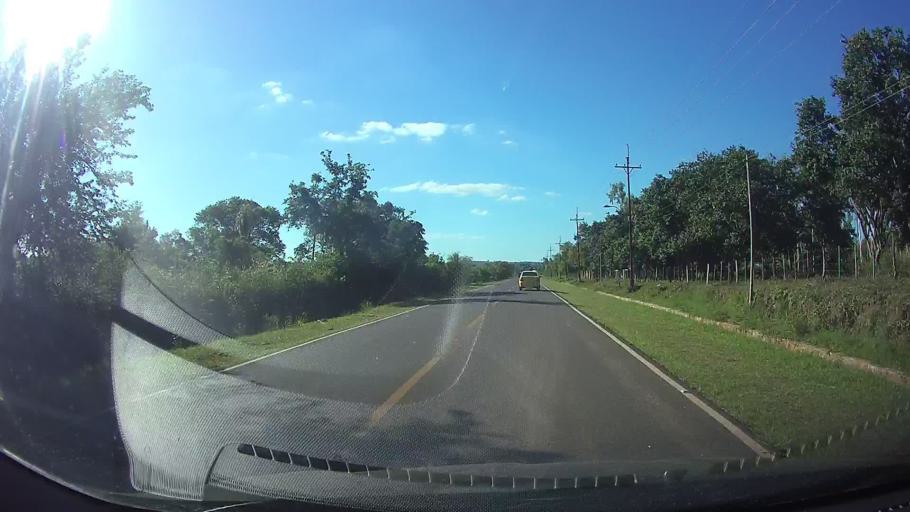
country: PY
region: Cordillera
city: Atyra
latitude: -25.2911
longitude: -57.1673
